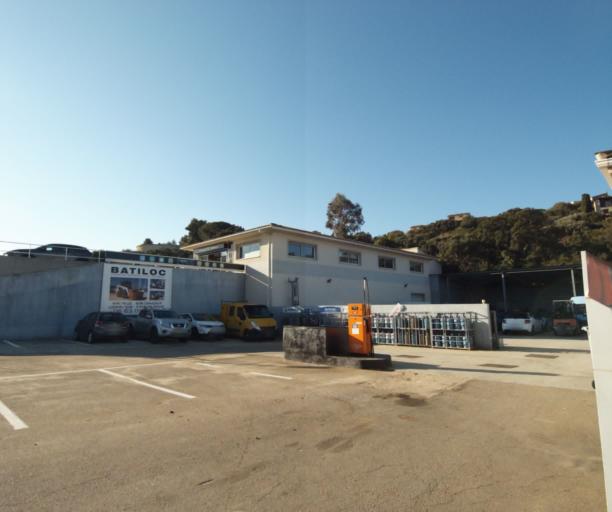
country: FR
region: Corsica
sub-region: Departement de la Corse-du-Sud
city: Propriano
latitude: 41.6704
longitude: 8.9135
